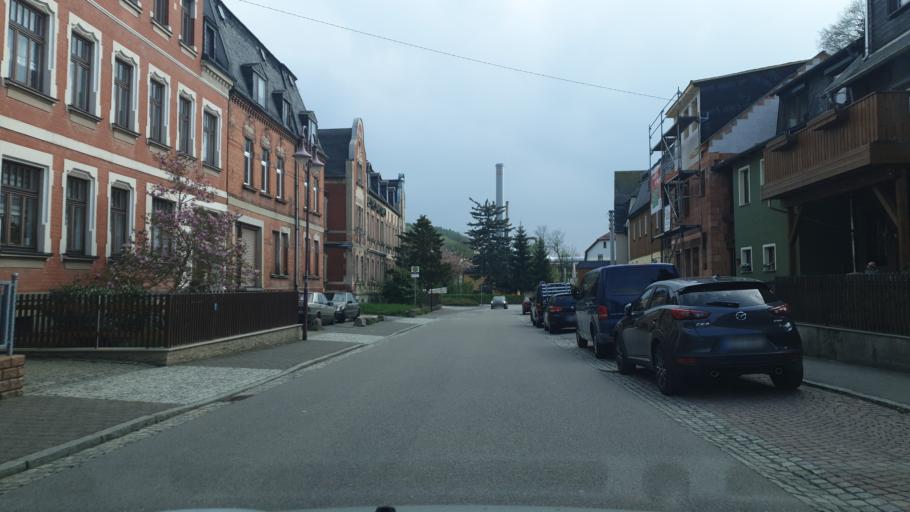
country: DE
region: Saxony
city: Lossnitz
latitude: 50.6164
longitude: 12.7270
